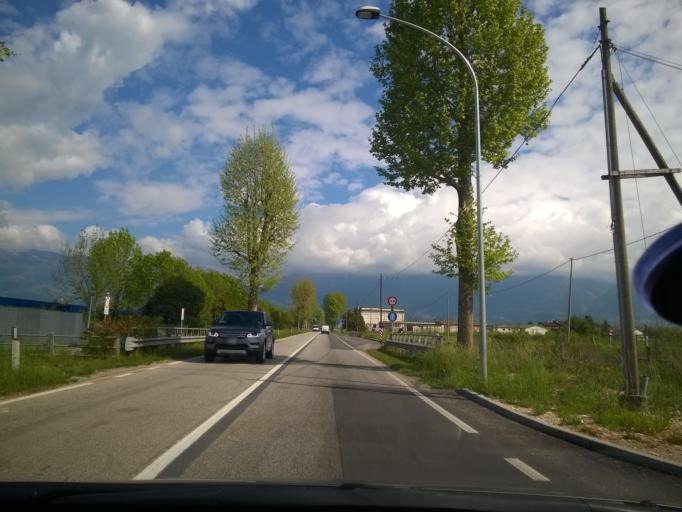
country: IT
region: Veneto
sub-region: Provincia di Treviso
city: Scomigo
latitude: 45.9445
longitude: 12.3232
